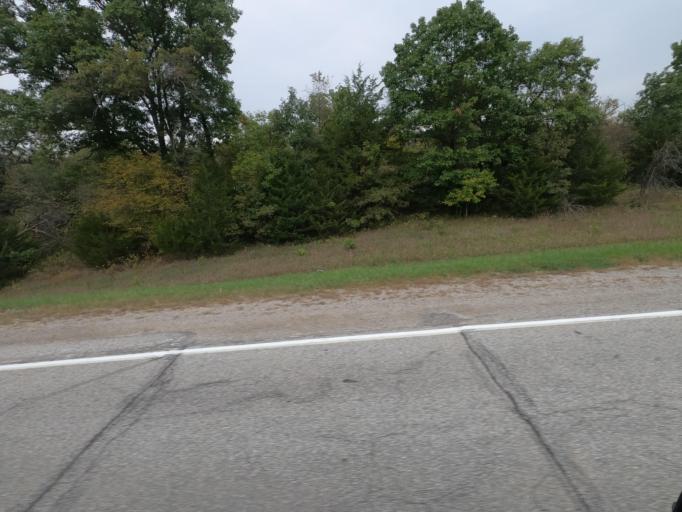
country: US
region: Iowa
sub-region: Van Buren County
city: Keosauqua
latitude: 40.8348
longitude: -91.9798
